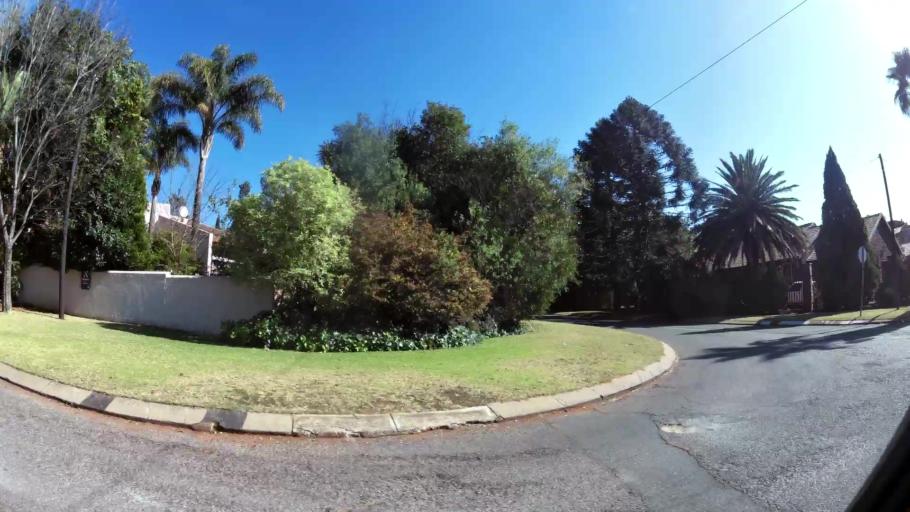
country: ZA
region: Gauteng
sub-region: City of Johannesburg Metropolitan Municipality
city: Roodepoort
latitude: -26.1194
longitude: 27.8601
